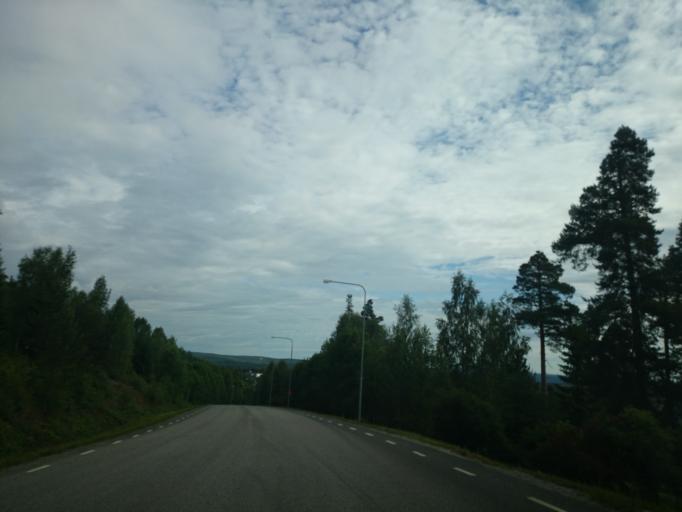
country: SE
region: Vaesternorrland
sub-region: Timra Kommun
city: Timra
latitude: 62.4880
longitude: 17.3196
